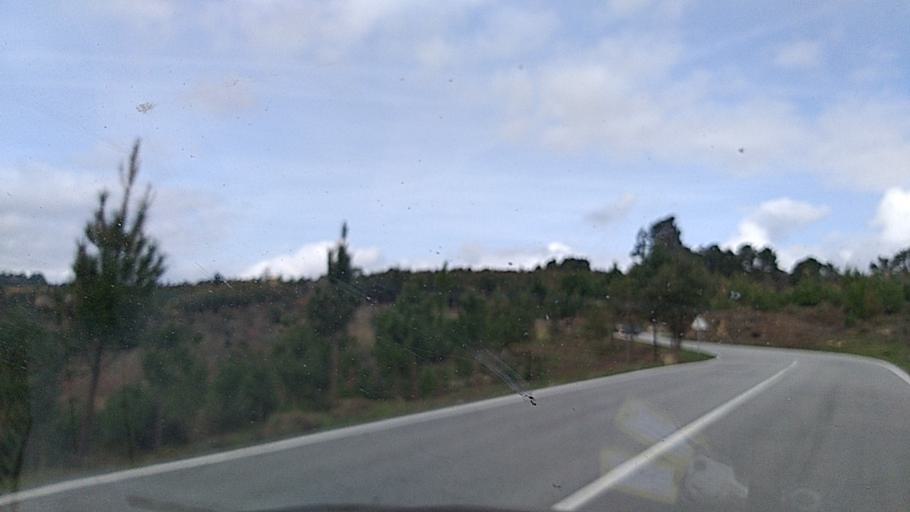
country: PT
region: Viseu
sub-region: Satao
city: Satao
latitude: 40.6665
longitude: -7.6839
